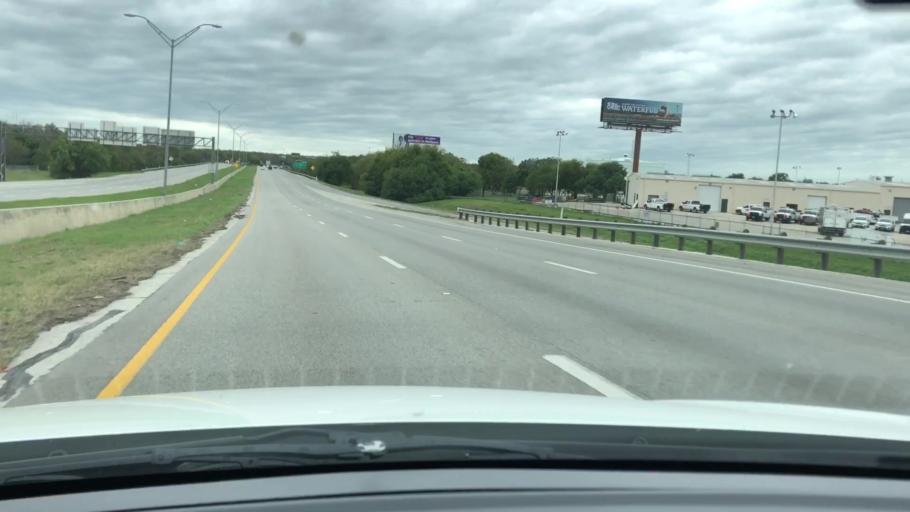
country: US
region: Texas
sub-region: Bexar County
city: Kirby
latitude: 29.4229
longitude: -98.4231
